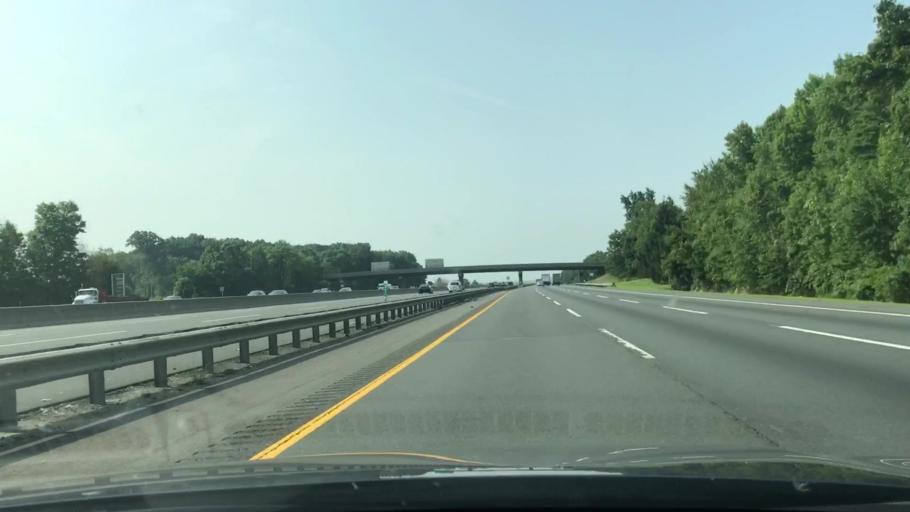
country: US
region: New Jersey
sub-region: Middlesex County
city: Helmetta
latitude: 40.4028
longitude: -74.4522
